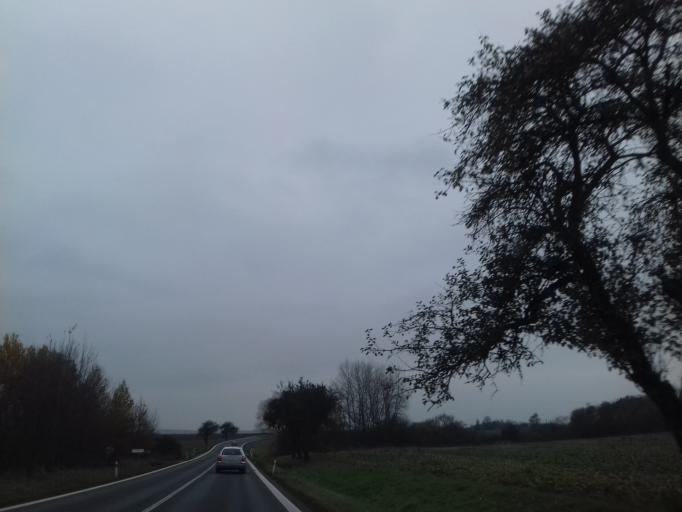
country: CZ
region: Plzensky
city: Chotesov
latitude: 49.6482
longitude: 13.1868
